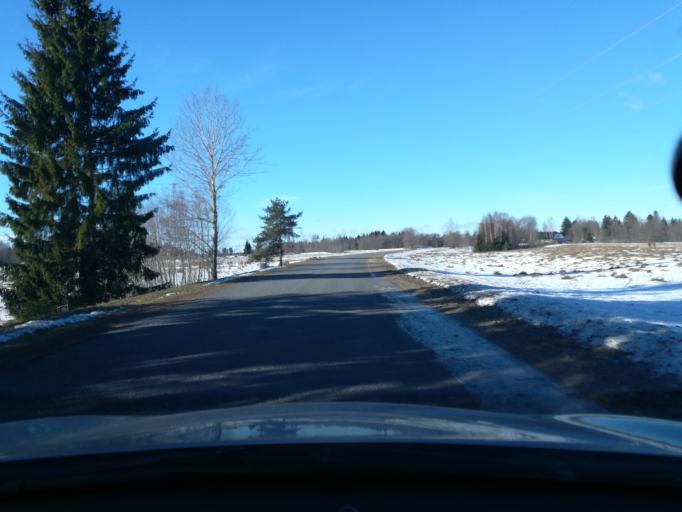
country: EE
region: Raplamaa
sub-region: Kohila vald
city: Kohila
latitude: 59.2344
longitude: 24.7616
